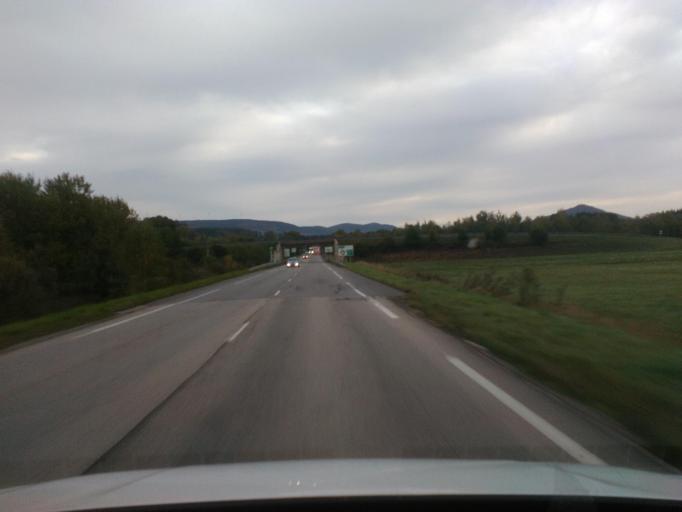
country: FR
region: Lorraine
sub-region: Departement des Vosges
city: Ban-de-Laveline
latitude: 48.2888
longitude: 7.0702
